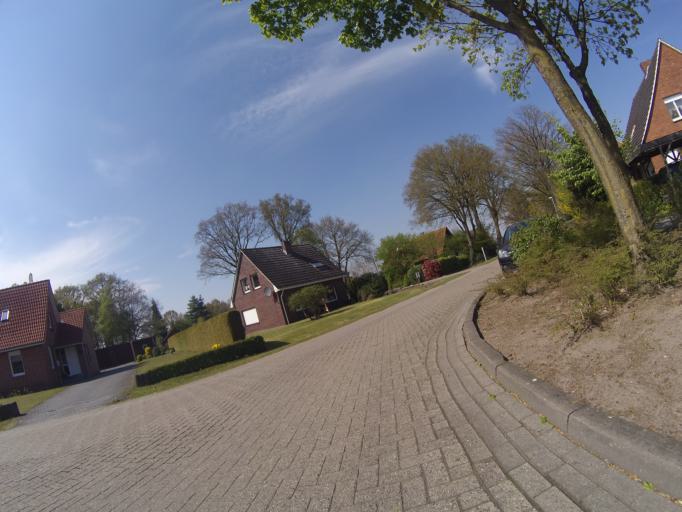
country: DE
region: Lower Saxony
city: Emlichheim
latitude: 52.6172
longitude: 6.8356
